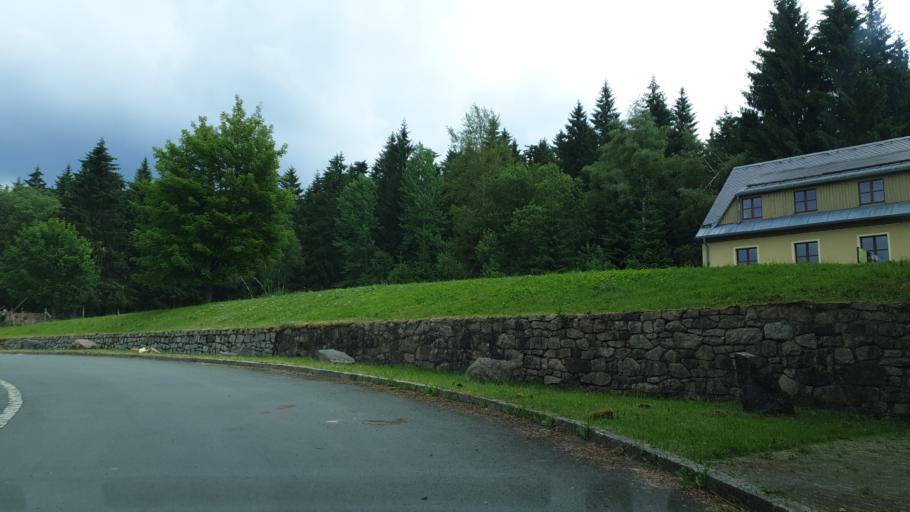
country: DE
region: Saxony
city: Tannenbergsthal
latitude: 50.4161
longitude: 12.4592
